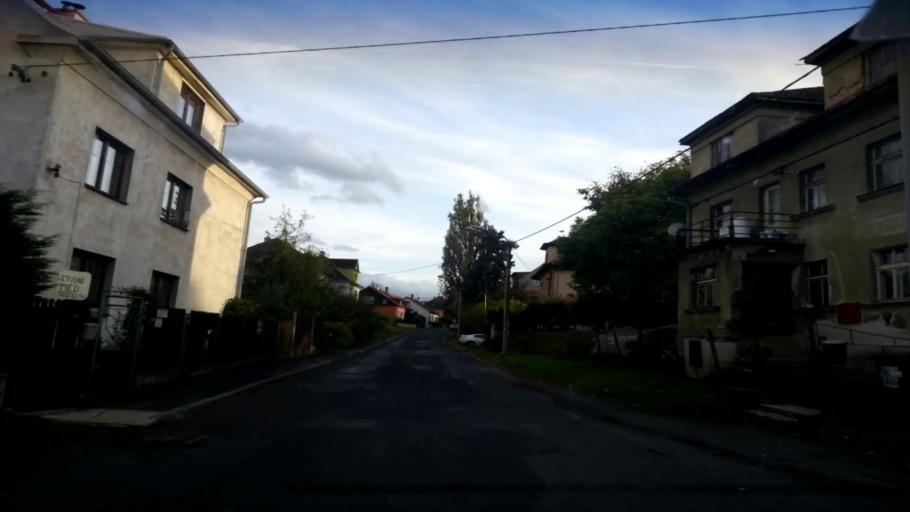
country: CZ
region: Karlovarsky
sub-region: Okres Cheb
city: Cheb
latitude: 50.0621
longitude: 12.3712
